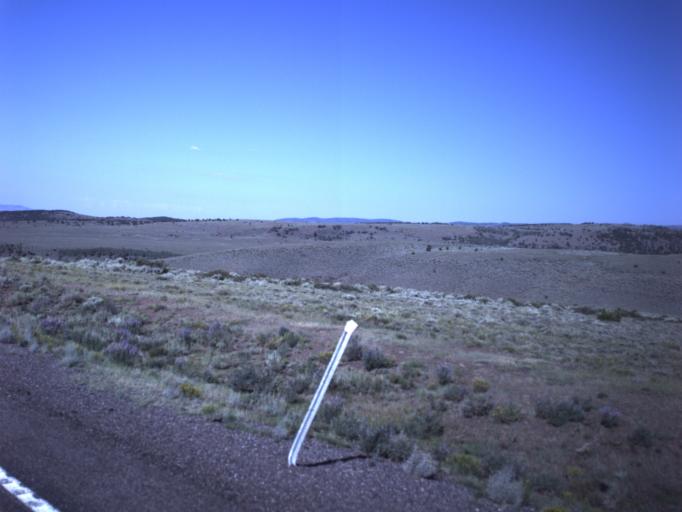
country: US
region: Utah
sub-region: Wayne County
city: Loa
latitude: 38.5507
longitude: -111.5098
